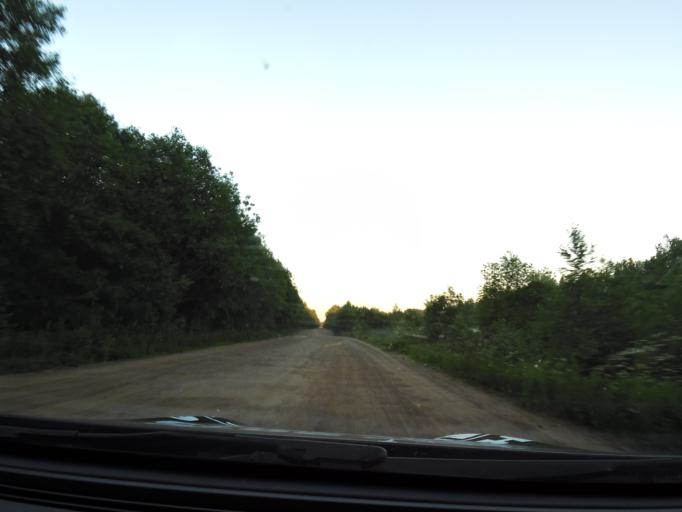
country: RU
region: Leningrad
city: Voznesen'ye
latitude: 60.9134
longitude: 35.4877
